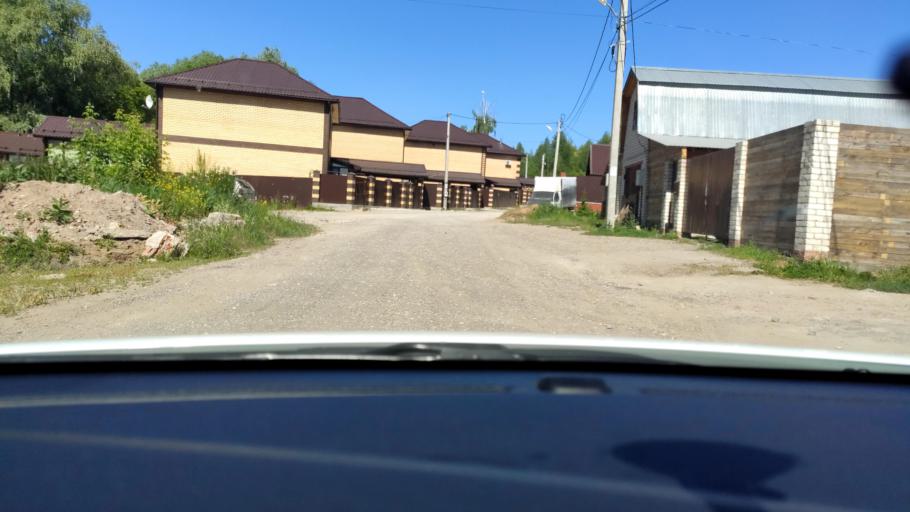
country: RU
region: Tatarstan
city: Stolbishchi
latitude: 55.7483
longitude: 49.2814
